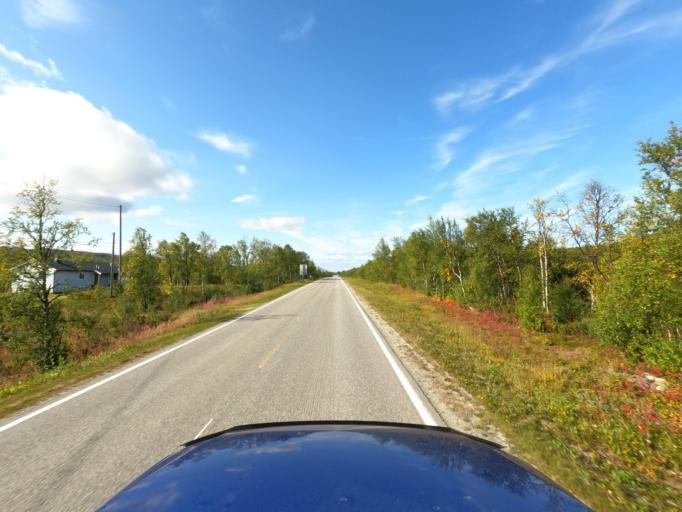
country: NO
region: Finnmark Fylke
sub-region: Porsanger
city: Lakselv
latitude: 69.7636
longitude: 25.1931
